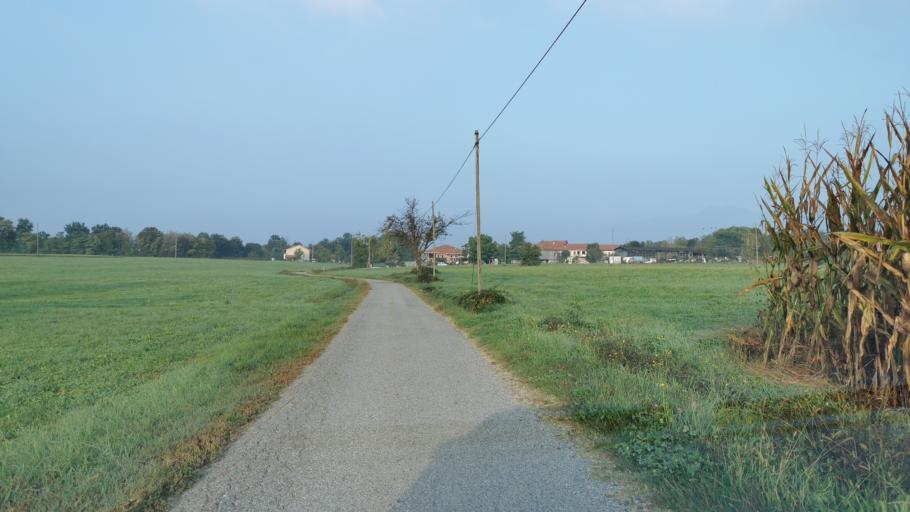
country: IT
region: Piedmont
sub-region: Provincia di Torino
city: Front
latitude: 45.2549
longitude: 7.6717
